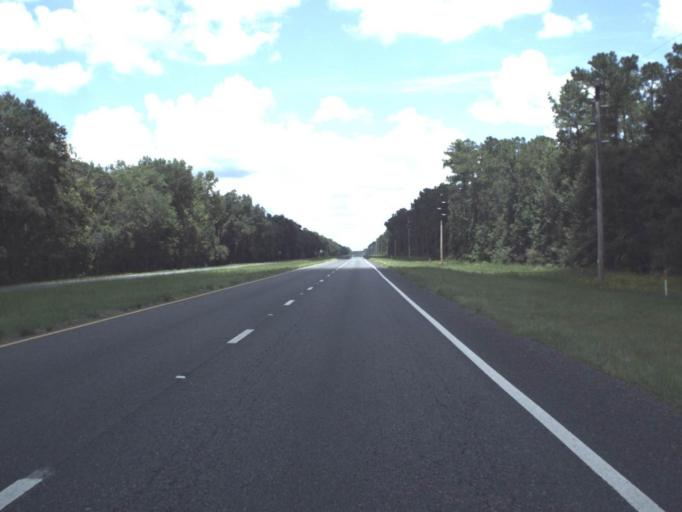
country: US
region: Florida
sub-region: Taylor County
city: Steinhatchee
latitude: 29.6901
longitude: -83.2716
